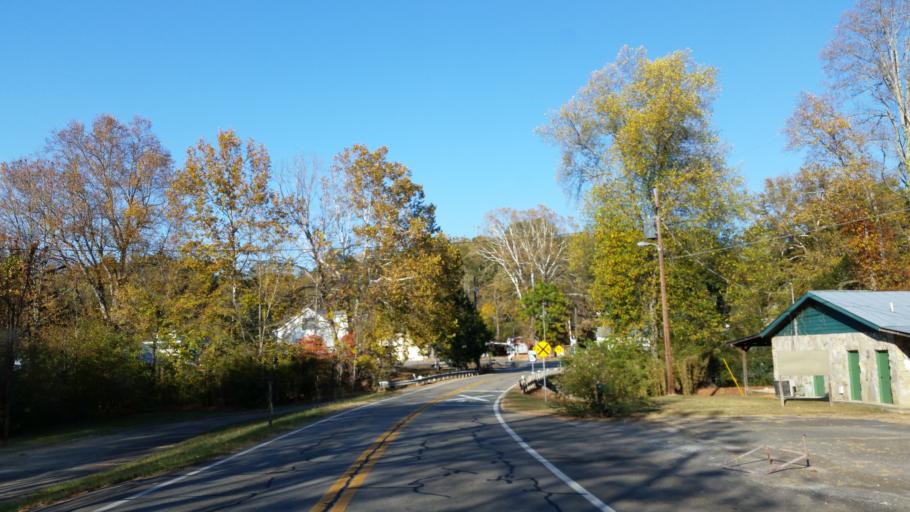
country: US
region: Georgia
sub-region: Pickens County
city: Jasper
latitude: 34.5084
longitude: -84.5063
